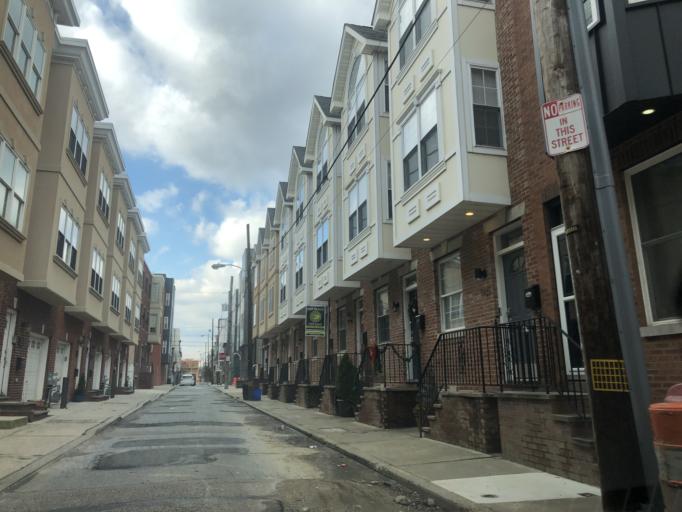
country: US
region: Pennsylvania
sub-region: Philadelphia County
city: Philadelphia
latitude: 39.9398
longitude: -75.1753
